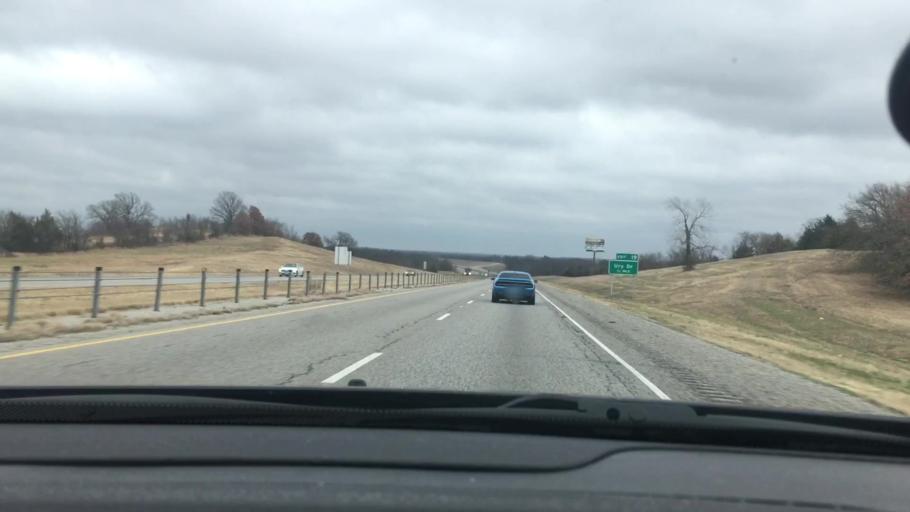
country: US
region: Oklahoma
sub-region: Bryan County
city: Durant
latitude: 34.0410
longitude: -96.3699
